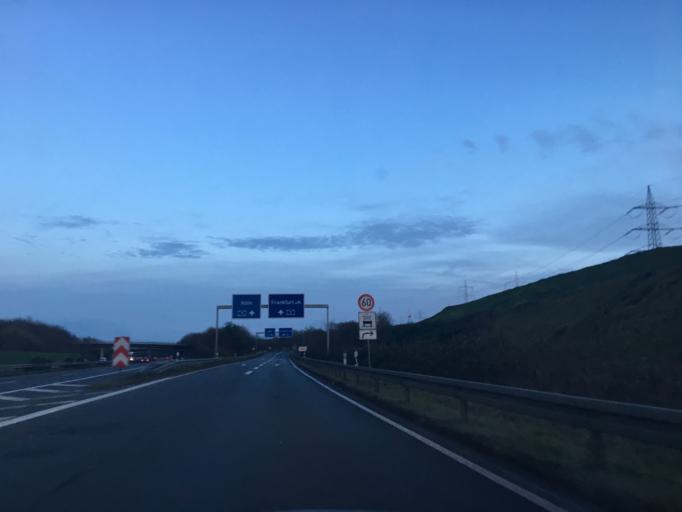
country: DE
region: North Rhine-Westphalia
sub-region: Regierungsbezirk Koln
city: Stossdorf
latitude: 50.7762
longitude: 7.2344
